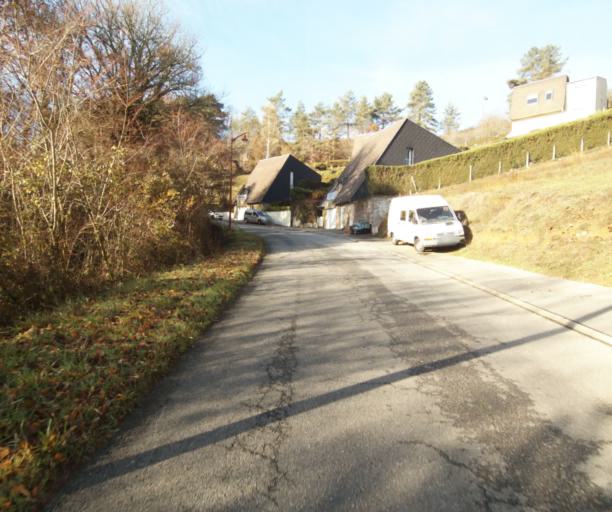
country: FR
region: Limousin
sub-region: Departement de la Correze
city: Laguenne
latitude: 45.2496
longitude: 1.7826
